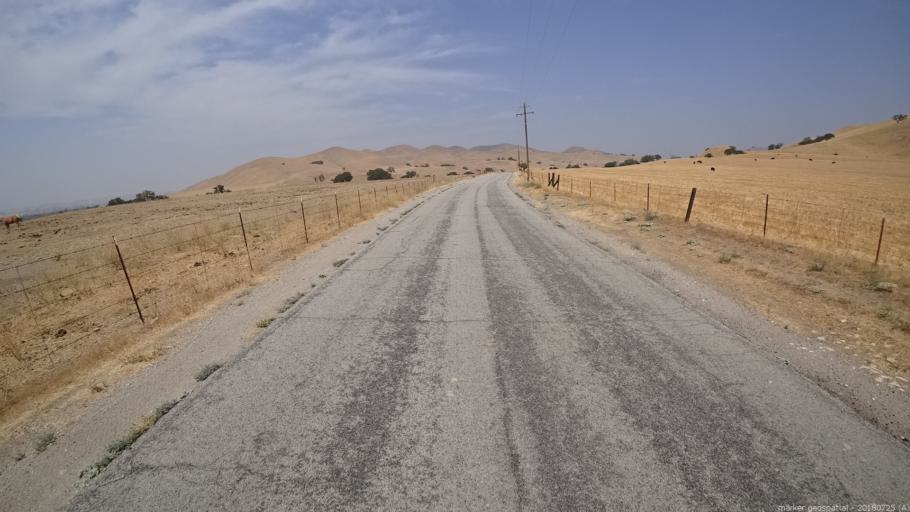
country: US
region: California
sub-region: San Luis Obispo County
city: San Miguel
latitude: 35.7751
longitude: -120.6942
